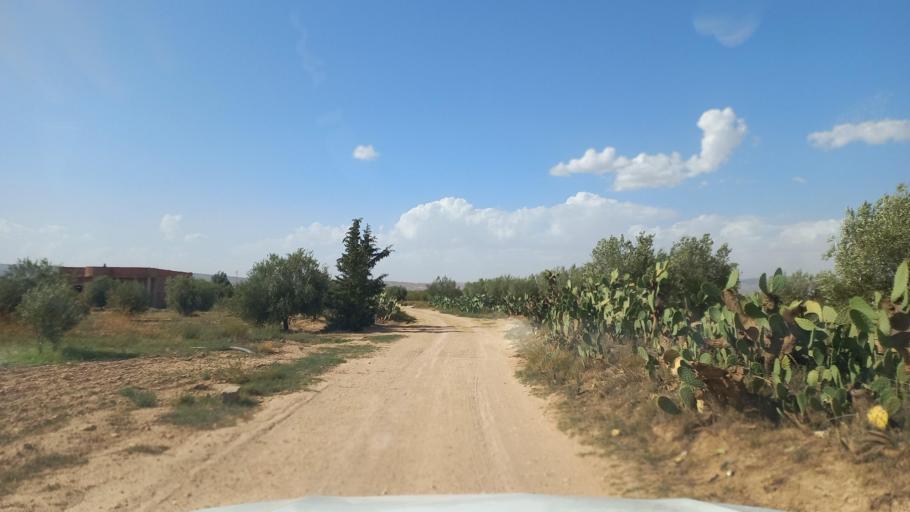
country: TN
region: Al Qasrayn
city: Sbiba
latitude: 35.3007
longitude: 9.0422
